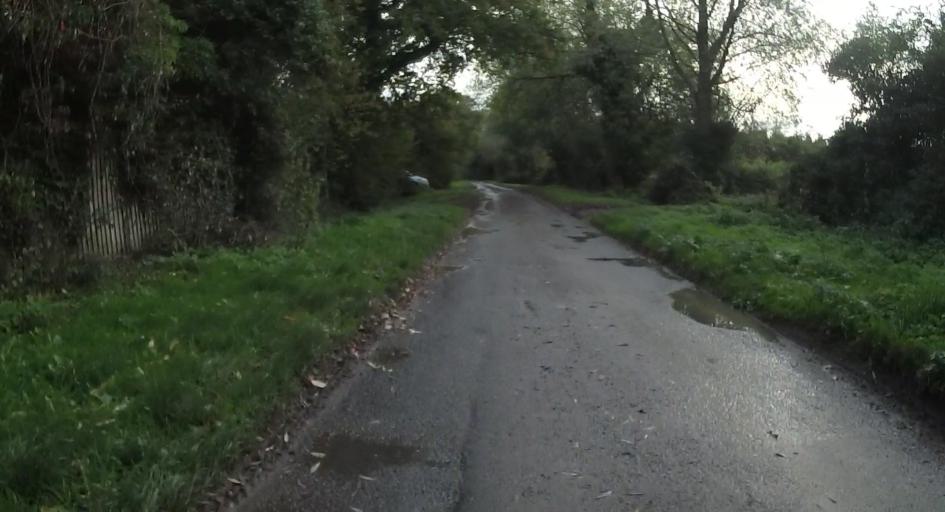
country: GB
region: England
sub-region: Wokingham
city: Swallowfield
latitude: 51.3756
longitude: -0.9599
